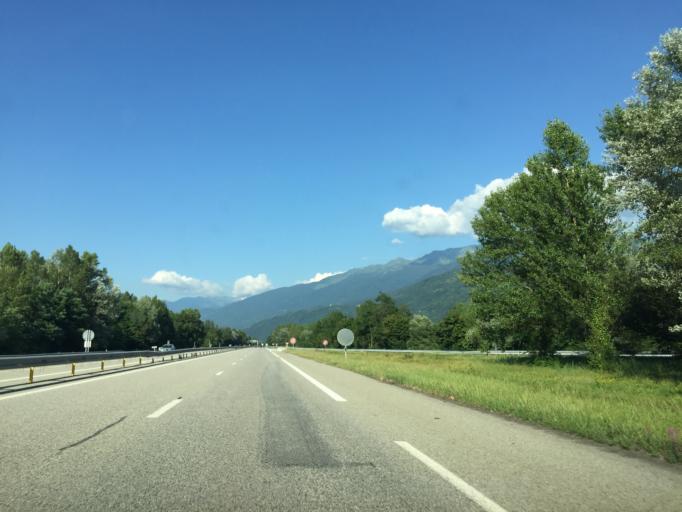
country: FR
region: Rhone-Alpes
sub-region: Departement de la Savoie
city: Aiton
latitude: 45.5673
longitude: 6.2229
